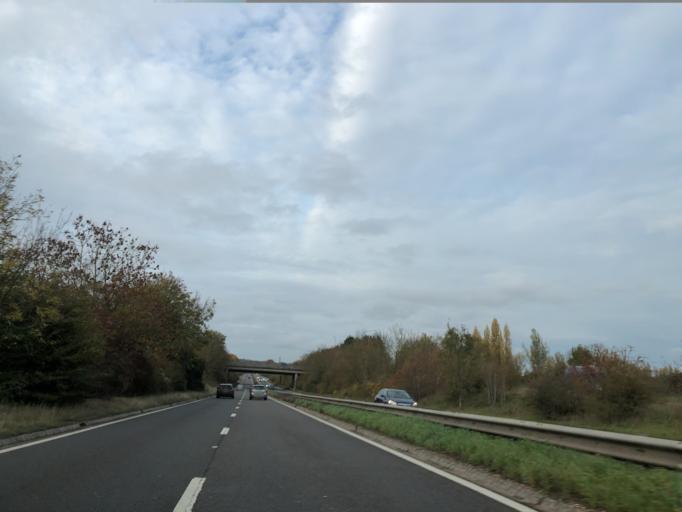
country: GB
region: England
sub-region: Buckinghamshire
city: Marlow
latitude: 51.5785
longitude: -0.7566
